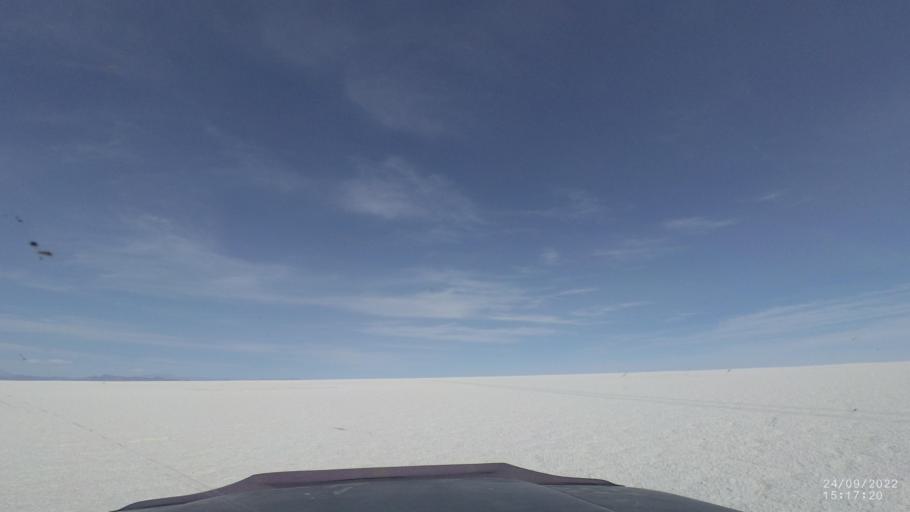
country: BO
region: Potosi
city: Colchani
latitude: -19.9885
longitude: -67.4280
